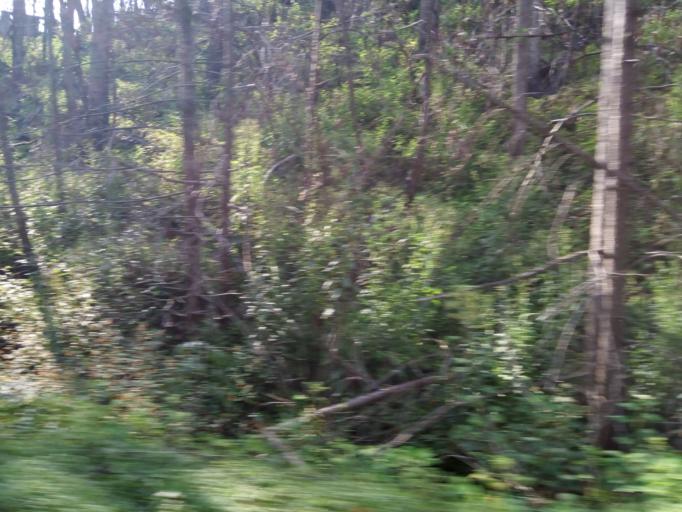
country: US
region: Tennessee
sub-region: Sevier County
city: Gatlinburg
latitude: 35.7268
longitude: -83.5312
